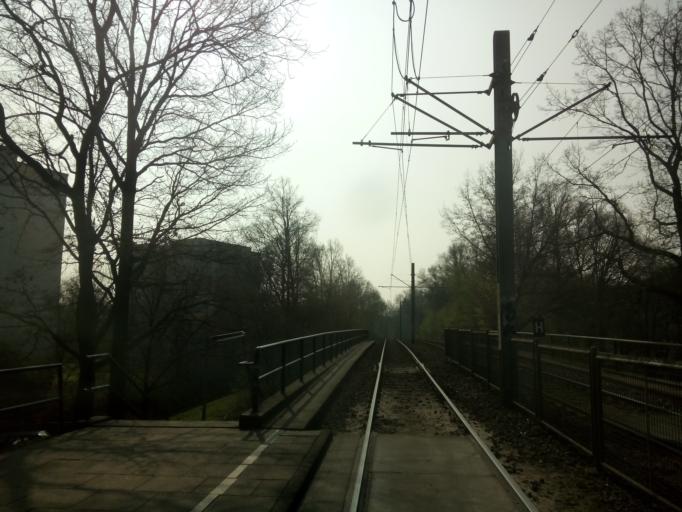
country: DE
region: Lower Saxony
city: Lilienthal
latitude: 53.0713
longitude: 8.9486
